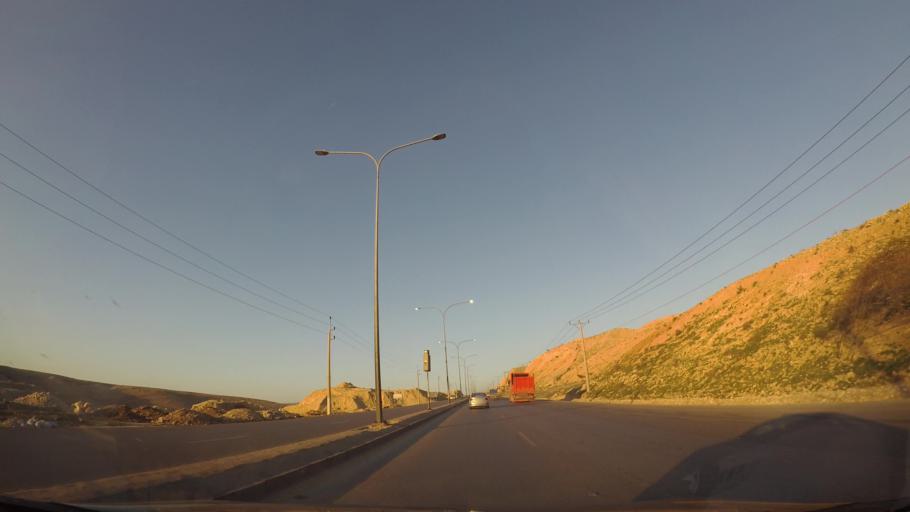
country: JO
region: Balqa
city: Yarqa
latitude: 31.8575
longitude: 35.7153
